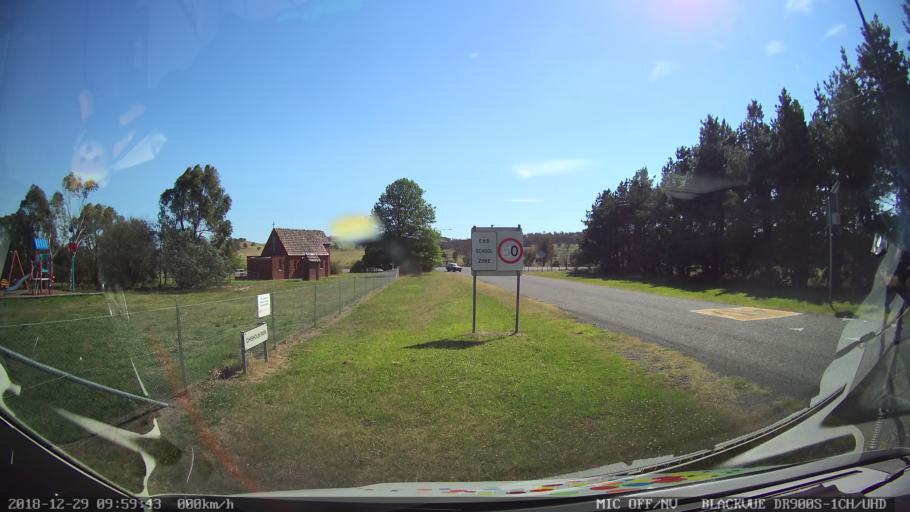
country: AU
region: New South Wales
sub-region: Goulburn Mulwaree
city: Goulburn
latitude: -34.7895
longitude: 149.4877
